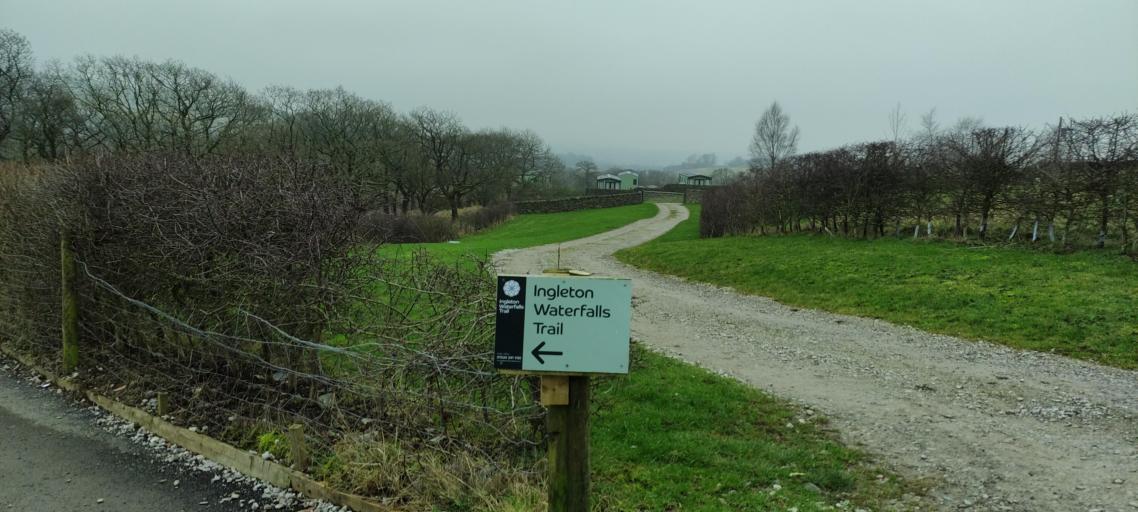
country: GB
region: England
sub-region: North Yorkshire
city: Ingleton
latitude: 54.1682
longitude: -2.4532
